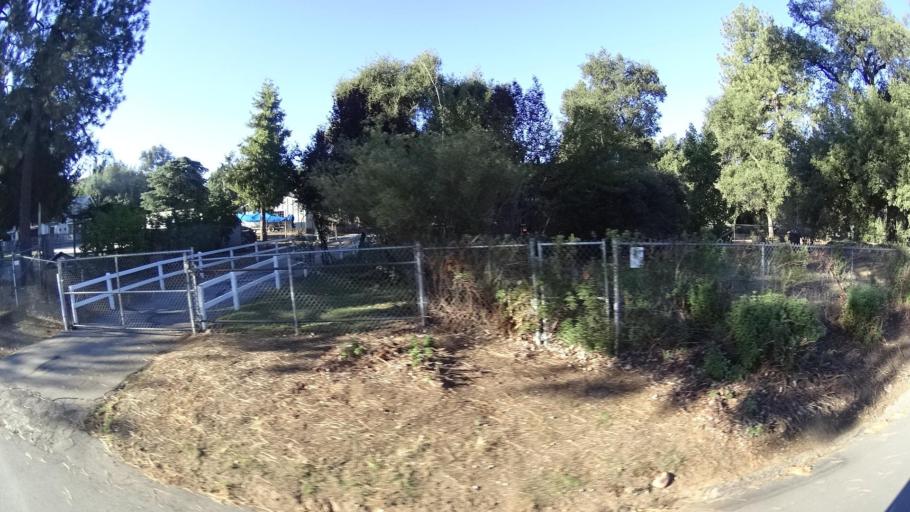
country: US
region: California
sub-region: San Diego County
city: Pine Valley
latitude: 32.8206
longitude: -116.5277
